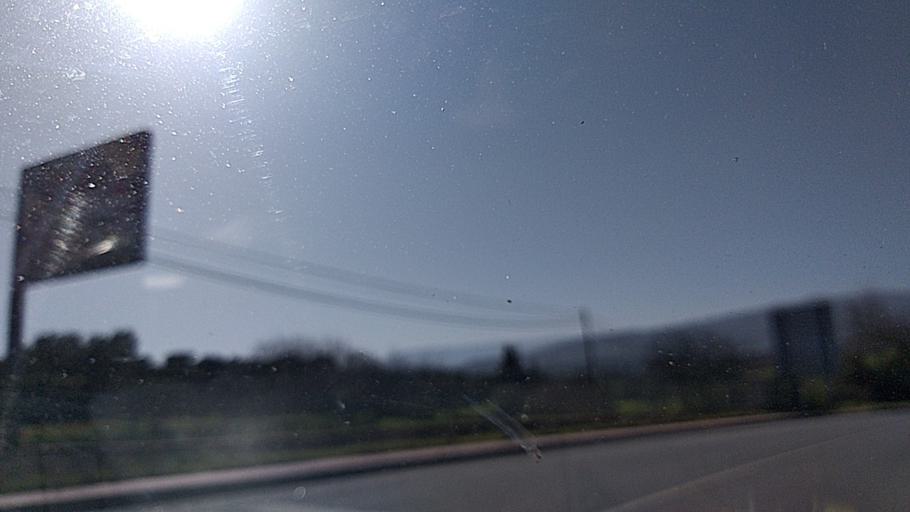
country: PT
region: Guarda
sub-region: Celorico da Beira
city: Celorico da Beira
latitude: 40.6566
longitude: -7.3809
